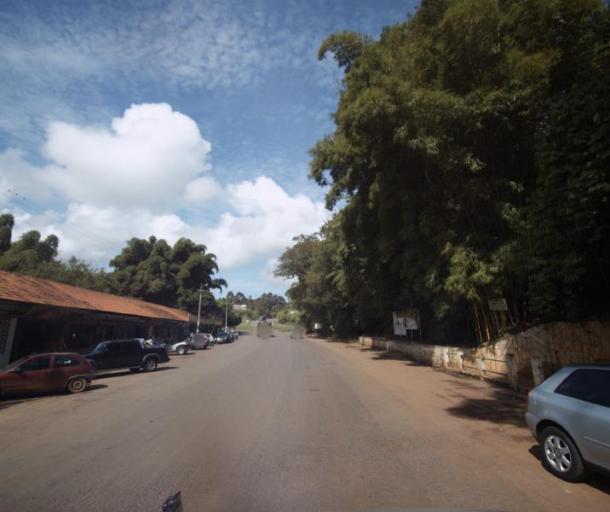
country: BR
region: Goias
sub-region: Pirenopolis
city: Pirenopolis
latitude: -15.9171
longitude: -48.8086
